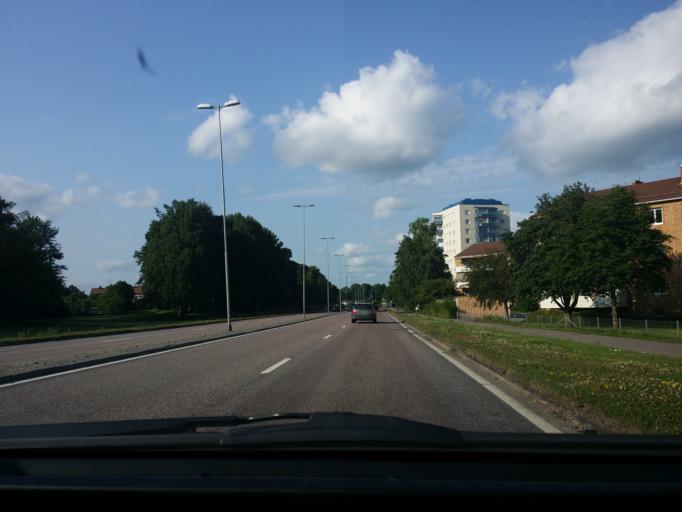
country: SE
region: Vaestmanland
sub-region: Vasteras
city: Vasteras
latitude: 59.6281
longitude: 16.5525
